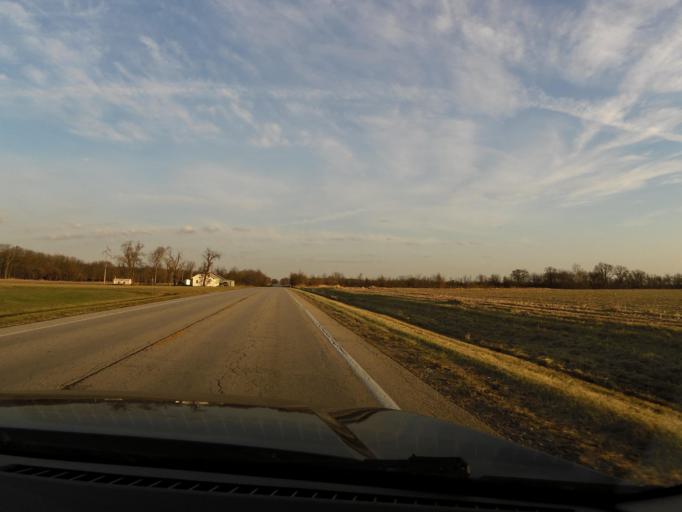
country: US
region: Illinois
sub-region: Fayette County
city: Vandalia
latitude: 38.8858
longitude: -89.0858
